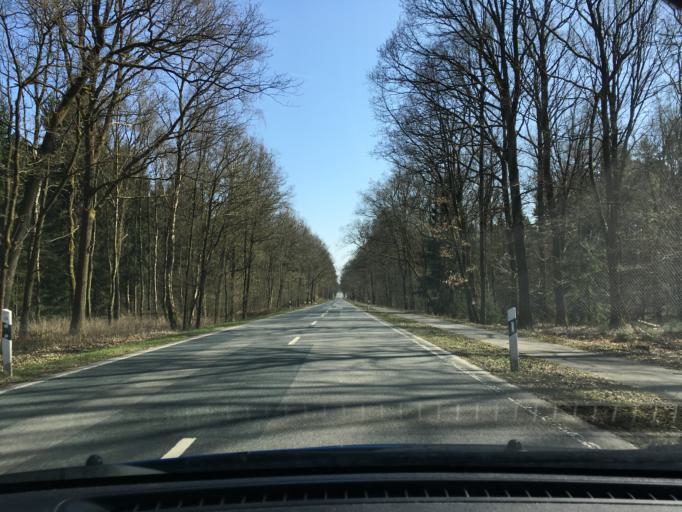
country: DE
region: Lower Saxony
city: Rehlingen
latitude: 53.0910
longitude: 10.2670
